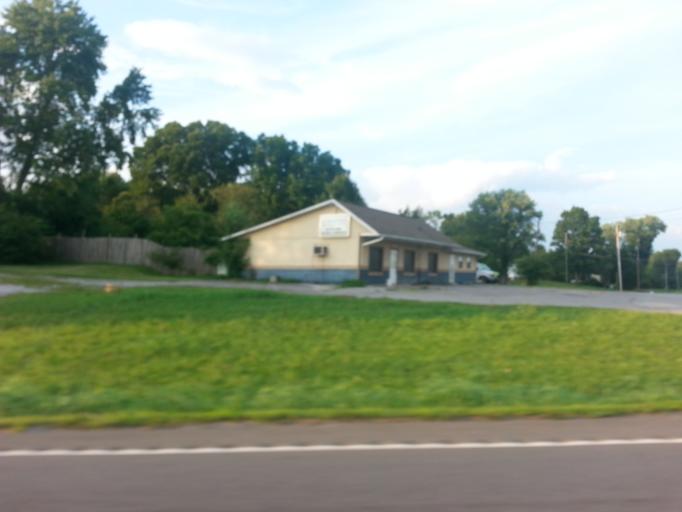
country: US
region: Tennessee
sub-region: Knox County
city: Knoxville
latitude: 36.0915
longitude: -83.9500
